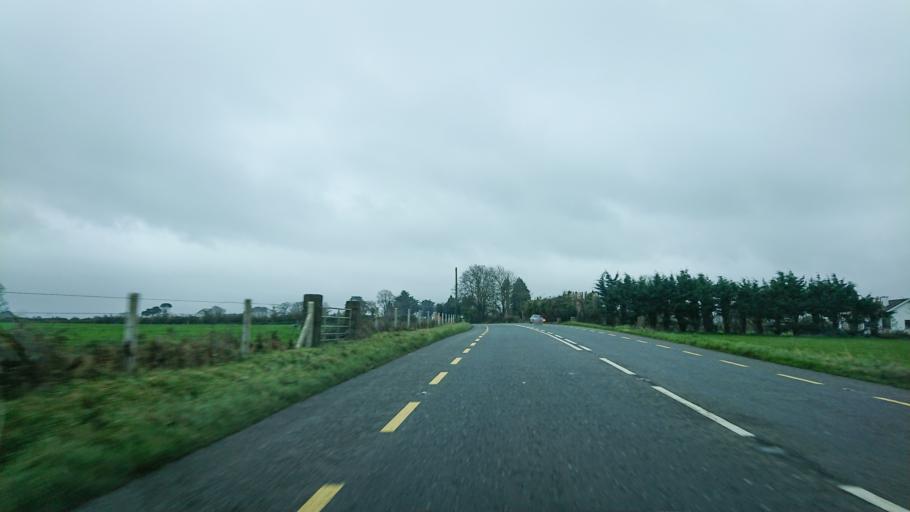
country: IE
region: Leinster
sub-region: Kilkenny
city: Mooncoin
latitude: 52.2833
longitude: -7.2087
